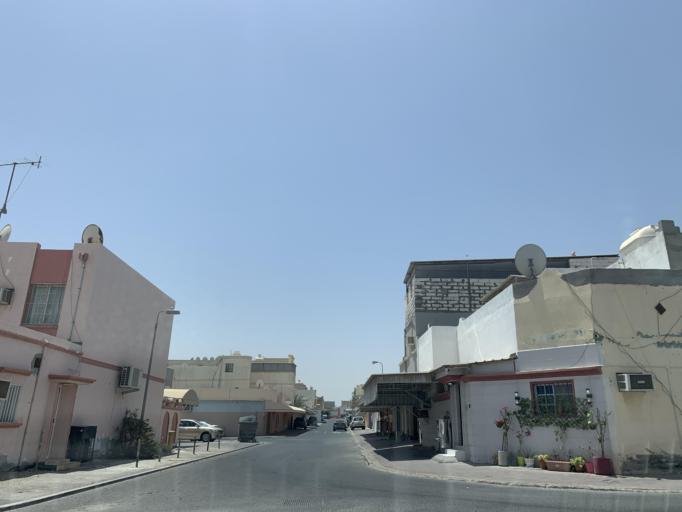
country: BH
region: Northern
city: Ar Rifa'
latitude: 26.1396
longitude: 50.5699
